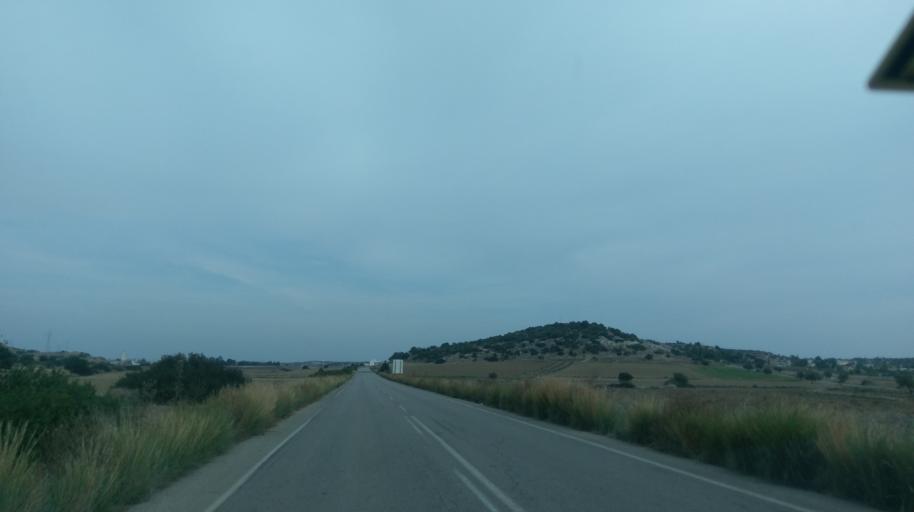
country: CY
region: Ammochostos
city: Leonarisso
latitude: 35.3971
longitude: 34.0672
